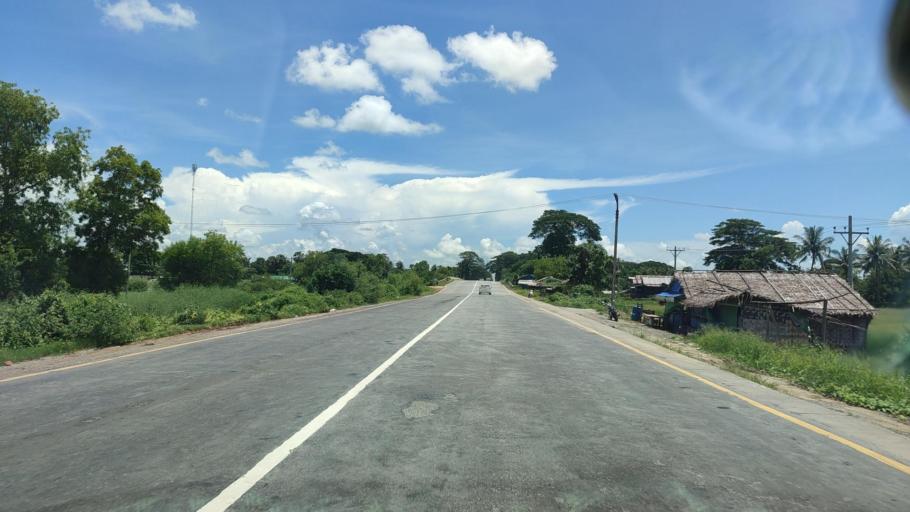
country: MM
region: Bago
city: Pyu
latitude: 18.3125
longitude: 96.5045
